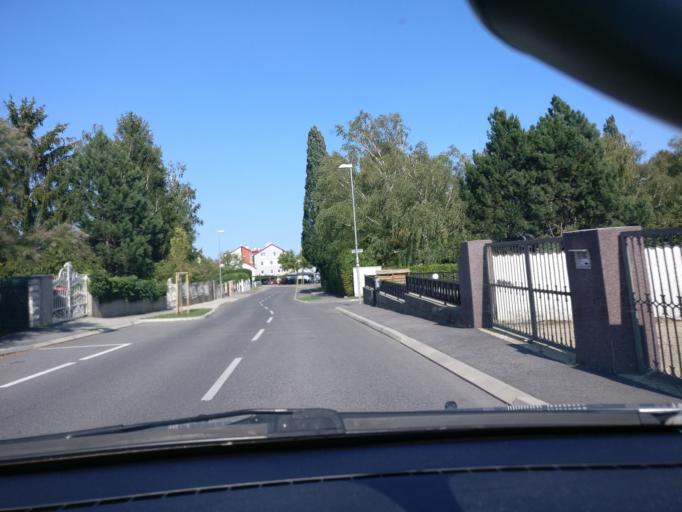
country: AT
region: Burgenland
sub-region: Politischer Bezirk Mattersburg
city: Mattersburg
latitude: 47.7332
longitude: 16.4021
